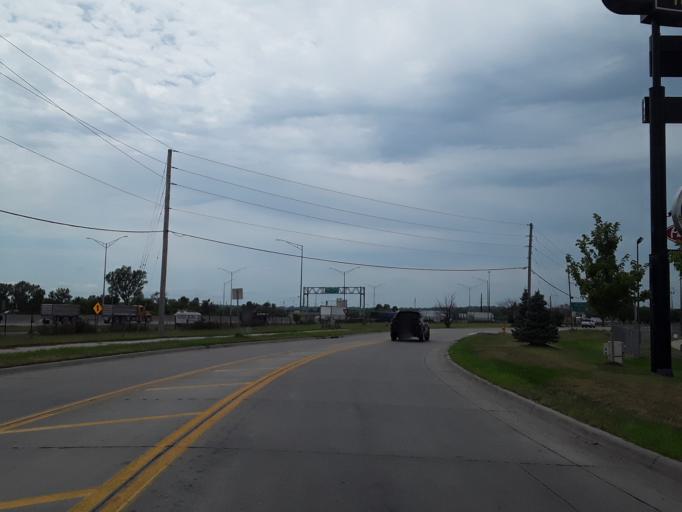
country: US
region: Iowa
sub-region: Pottawattamie County
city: Council Bluffs
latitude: 41.2336
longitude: -95.8816
